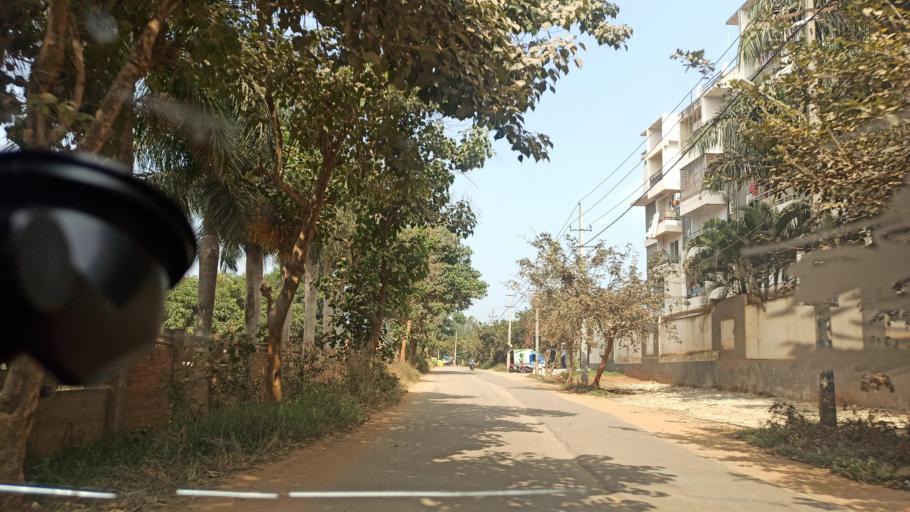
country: IN
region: Karnataka
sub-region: Bangalore Urban
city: Yelahanka
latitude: 13.0960
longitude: 77.6185
